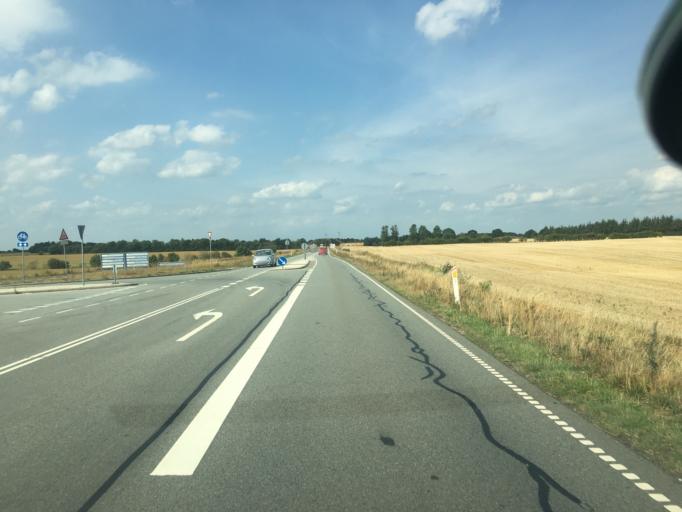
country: DK
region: South Denmark
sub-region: Aabenraa Kommune
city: Krusa
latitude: 54.9393
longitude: 9.3732
